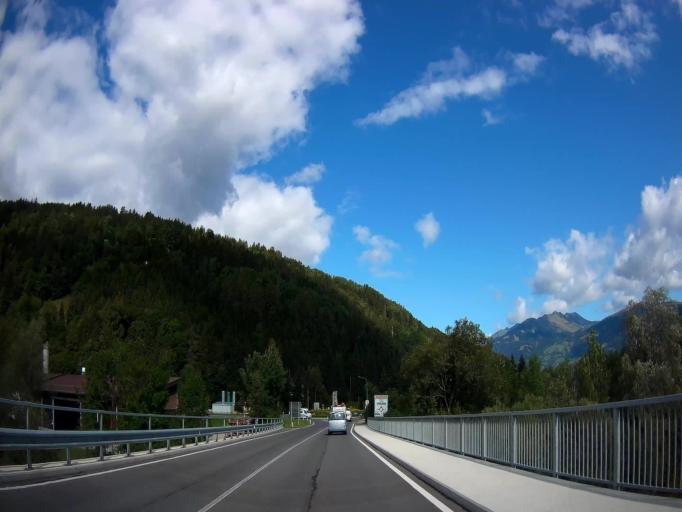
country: AT
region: Carinthia
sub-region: Politischer Bezirk Spittal an der Drau
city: Gmuend
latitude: 46.9027
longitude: 13.5326
